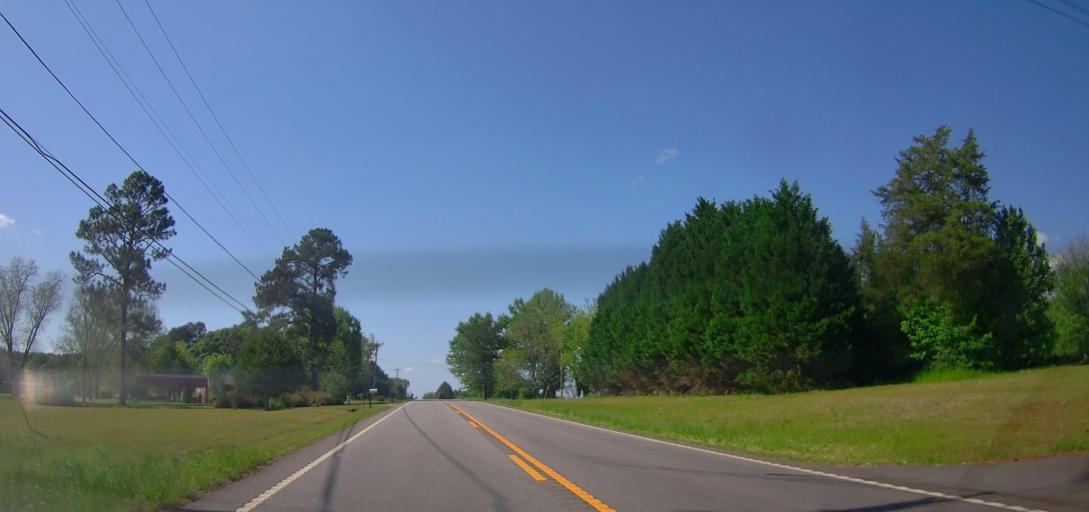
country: US
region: Georgia
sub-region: Morgan County
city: Madison
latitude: 33.6225
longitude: -83.4832
